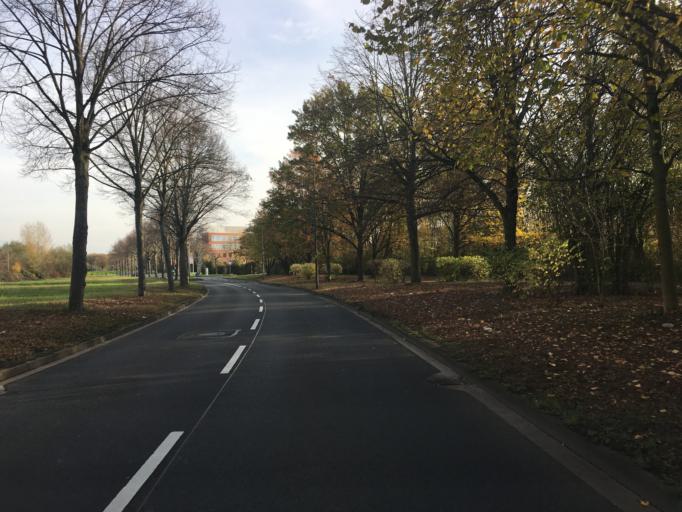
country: DE
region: North Rhine-Westphalia
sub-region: Regierungsbezirk Koln
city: Merheim
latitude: 50.9584
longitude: 7.0465
